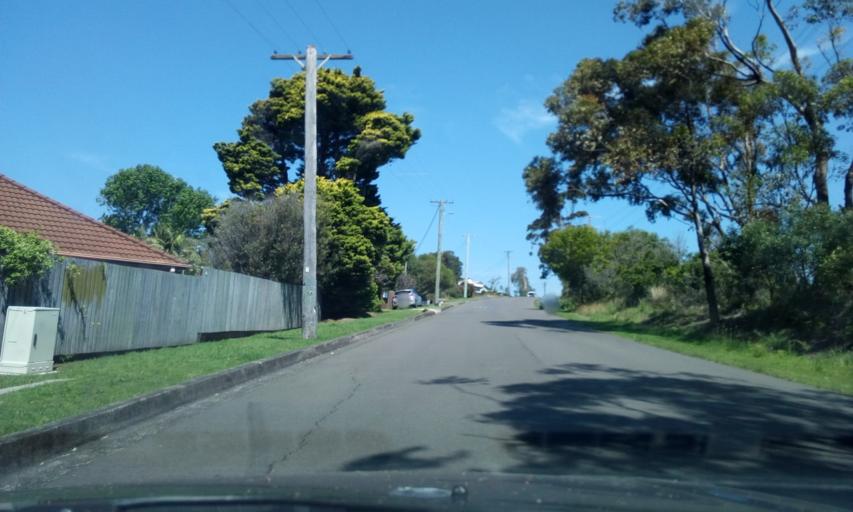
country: AU
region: New South Wales
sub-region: Wollongong
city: Bulli
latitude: -34.3424
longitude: 150.9161
